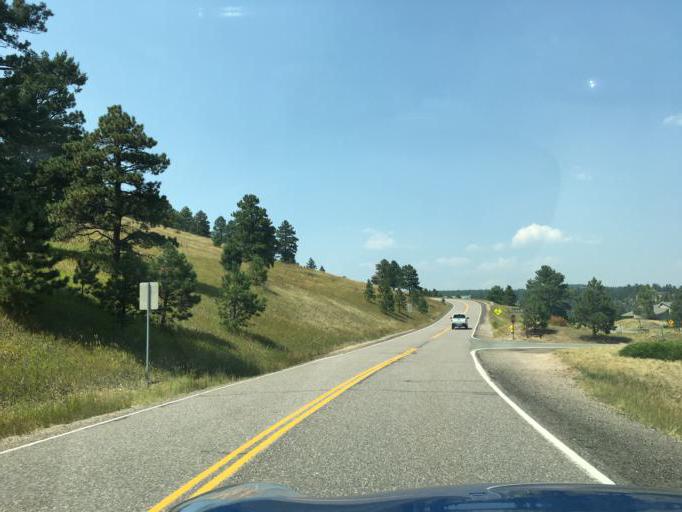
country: US
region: Colorado
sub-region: Jefferson County
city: Genesee
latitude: 39.7027
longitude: -105.2744
